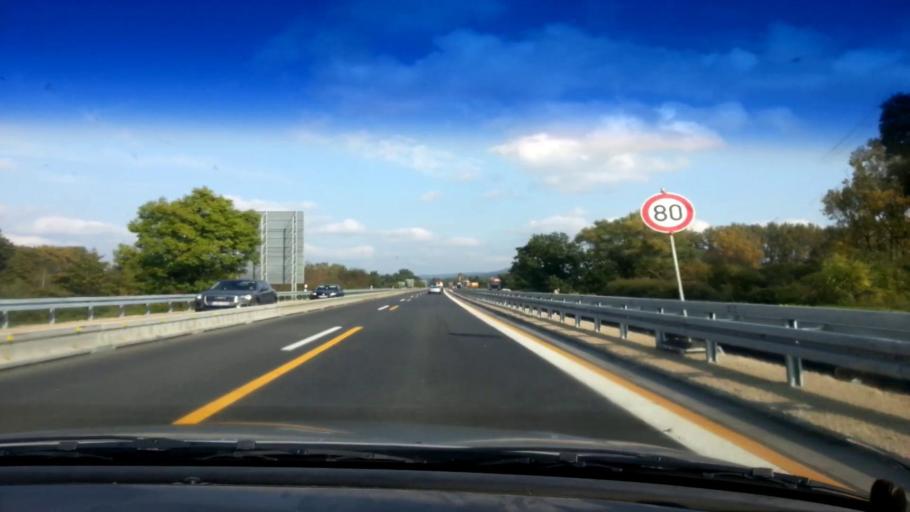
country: DE
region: Bavaria
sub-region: Upper Franconia
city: Gundelsheim
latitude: 49.9313
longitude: 10.9299
